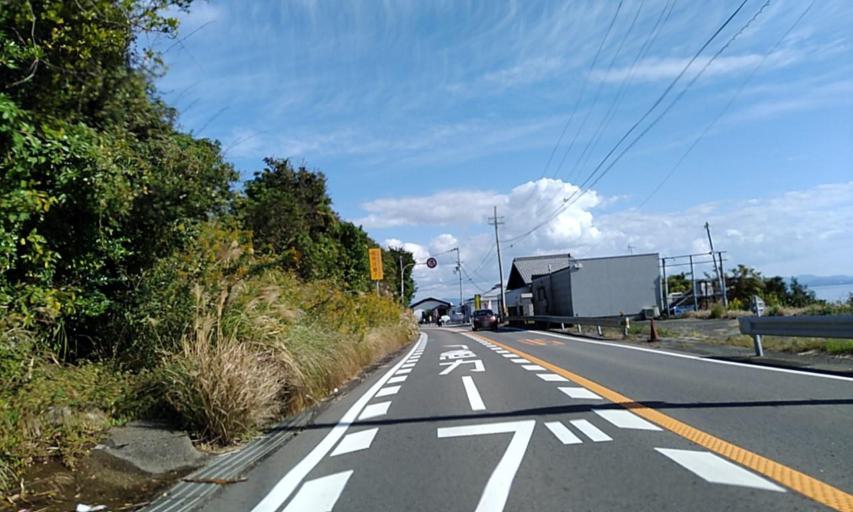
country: JP
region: Wakayama
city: Tanabe
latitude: 33.7810
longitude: 135.2435
